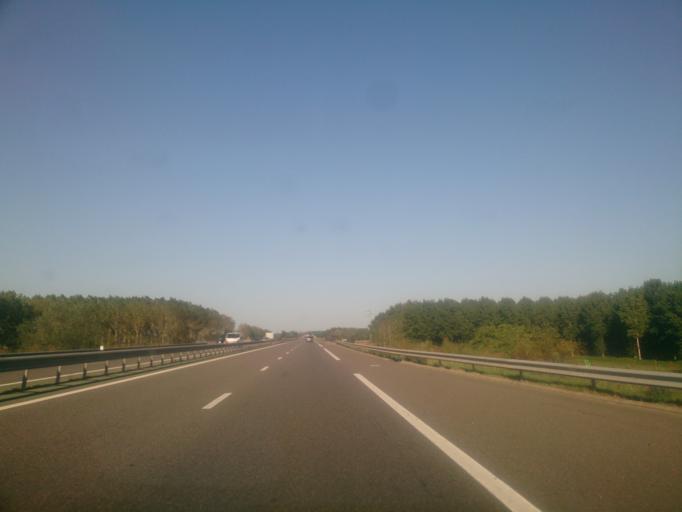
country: FR
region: Midi-Pyrenees
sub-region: Departement du Tarn-et-Garonne
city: Albias
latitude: 44.0957
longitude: 1.4353
